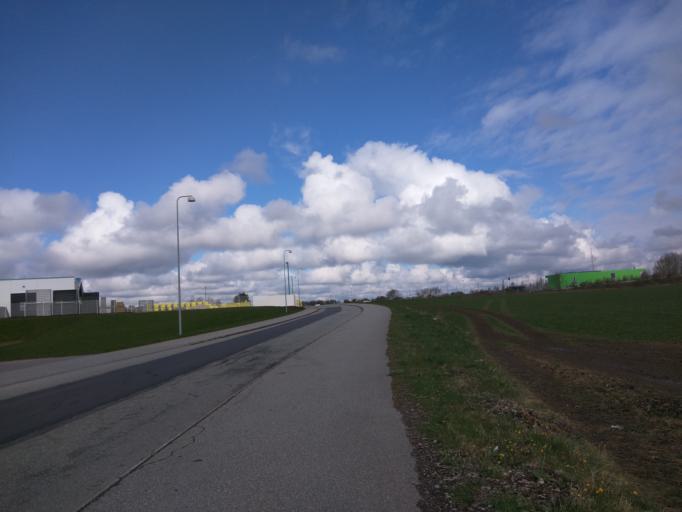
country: DK
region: South Denmark
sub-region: Fredericia Kommune
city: Snoghoj
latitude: 55.5374
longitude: 9.7023
